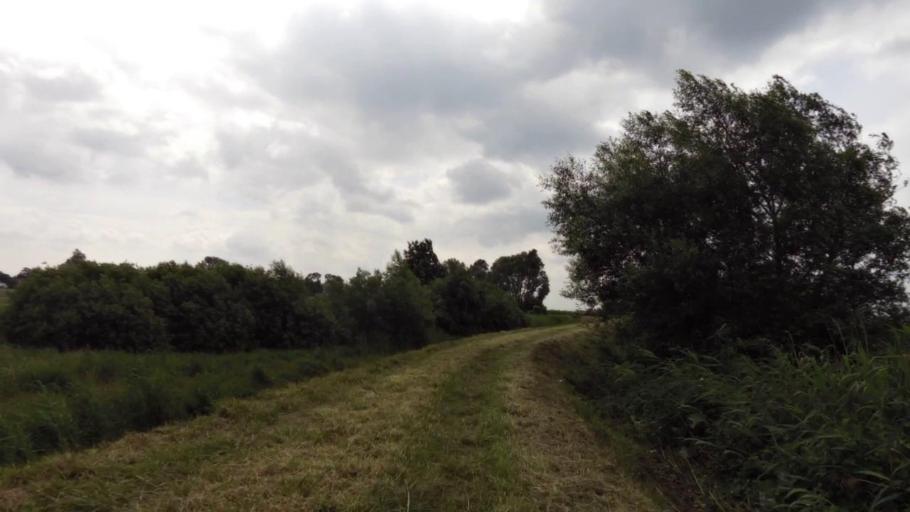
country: PL
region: West Pomeranian Voivodeship
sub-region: Powiat policki
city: Police
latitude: 53.5106
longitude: 14.6952
